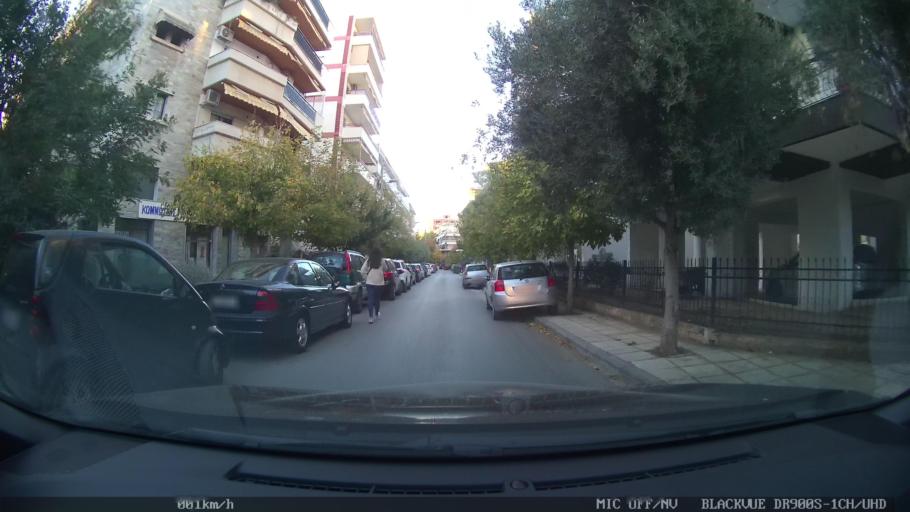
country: GR
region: Central Macedonia
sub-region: Nomos Thessalonikis
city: Pylaia
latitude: 40.6041
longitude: 22.9807
